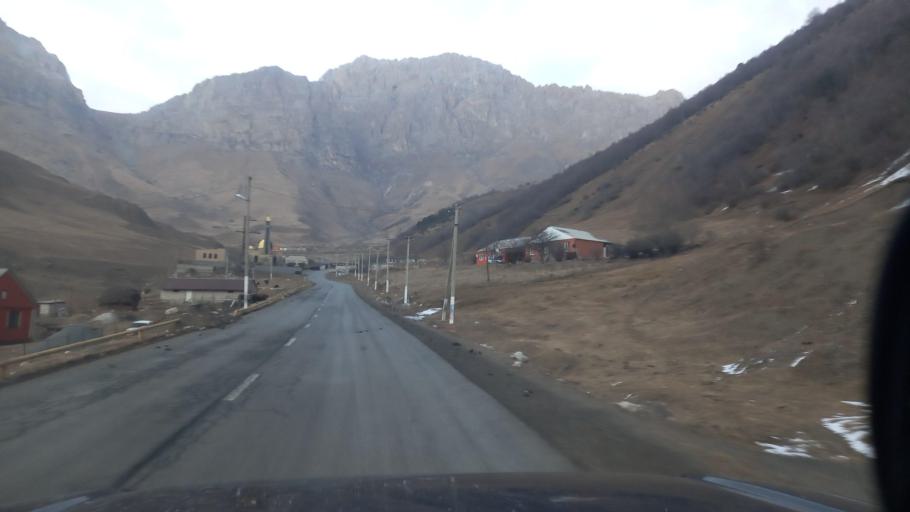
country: RU
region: Ingushetiya
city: Dzhayrakh
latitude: 42.8130
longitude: 44.8125
